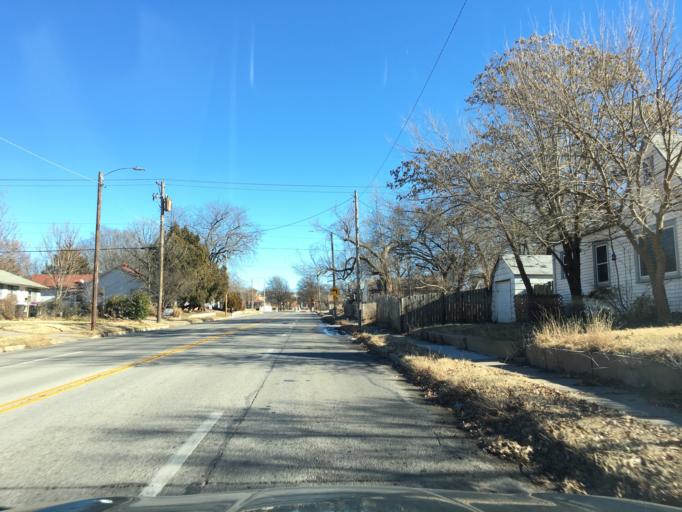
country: US
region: Kansas
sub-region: Sedgwick County
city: Wichita
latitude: 37.6718
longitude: -97.2967
